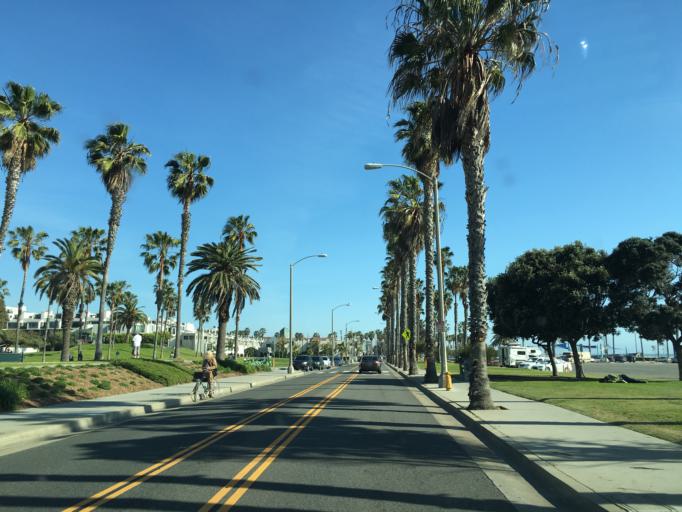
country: US
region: California
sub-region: Los Angeles County
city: Santa Monica
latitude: 33.9995
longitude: -118.4845
